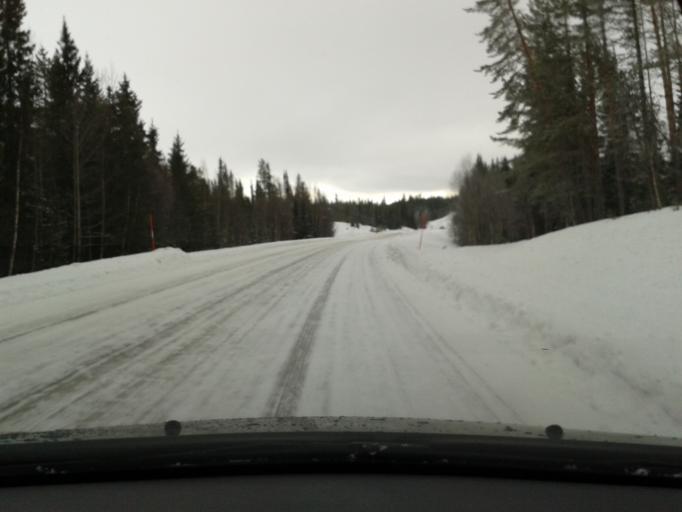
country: SE
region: Vaesterbotten
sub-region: Vilhelmina Kommun
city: Sjoberg
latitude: 64.8256
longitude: 15.9580
